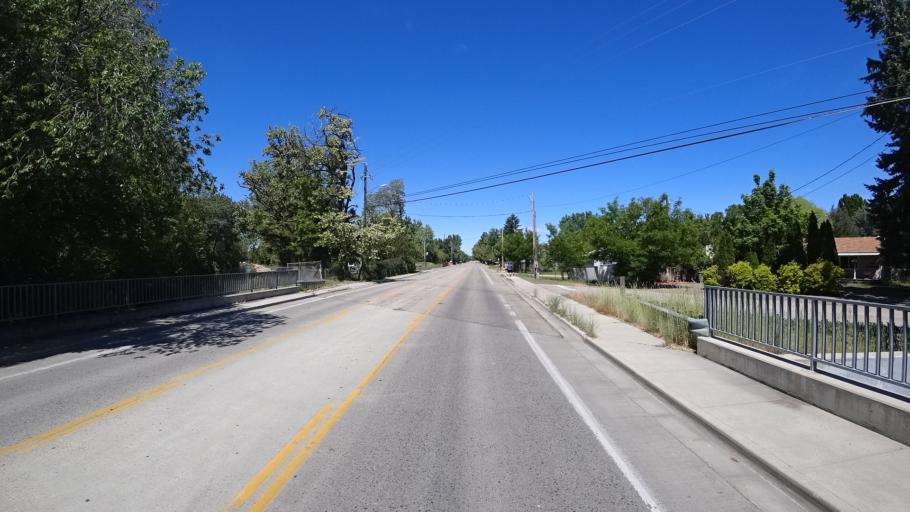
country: US
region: Idaho
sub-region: Ada County
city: Boise
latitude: 43.5744
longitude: -116.1646
